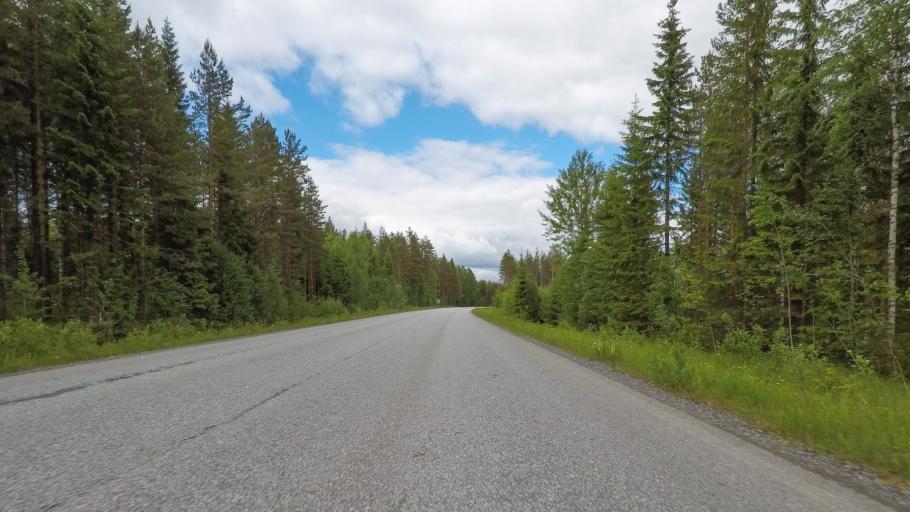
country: FI
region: Central Finland
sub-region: Jyvaeskylae
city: Toivakka
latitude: 62.1909
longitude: 26.2024
